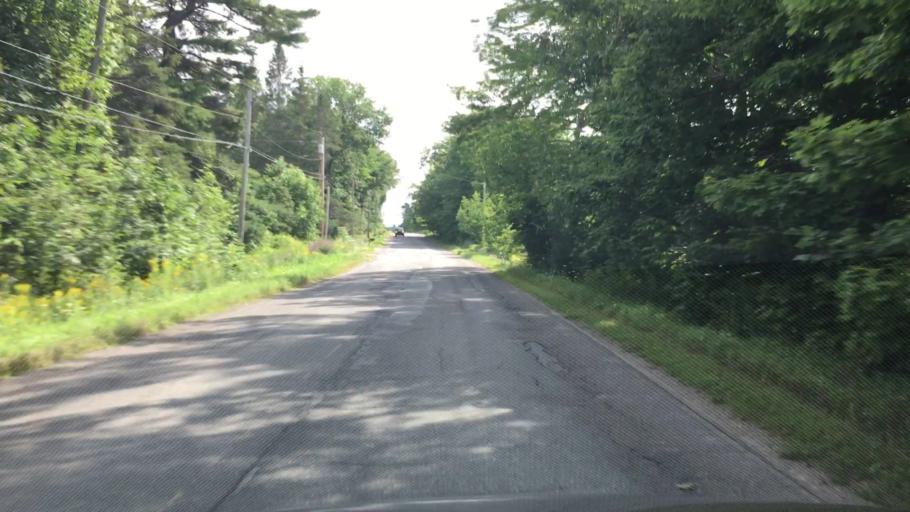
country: US
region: Maine
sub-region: Penobscot County
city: Hampden
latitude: 44.7259
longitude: -68.8642
